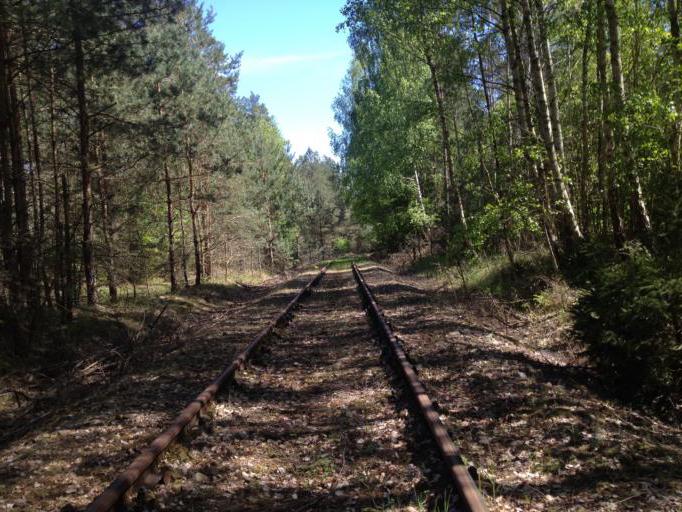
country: DE
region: Brandenburg
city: Templin
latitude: 53.1508
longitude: 13.4018
